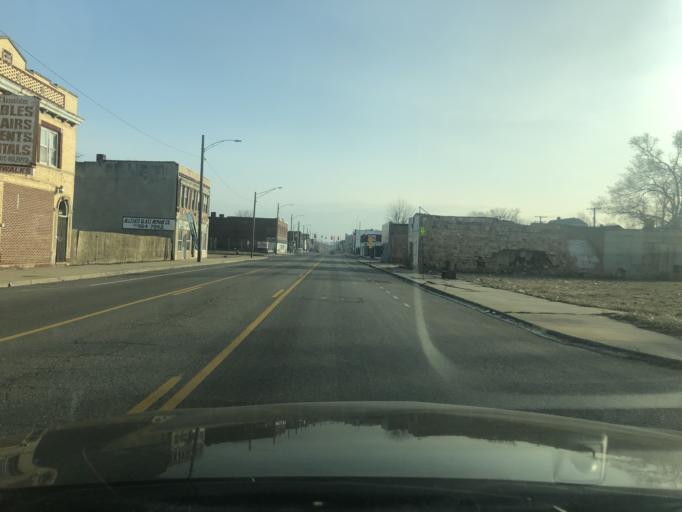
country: US
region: Michigan
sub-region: Wayne County
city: Highland Park
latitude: 42.4027
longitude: -83.1380
